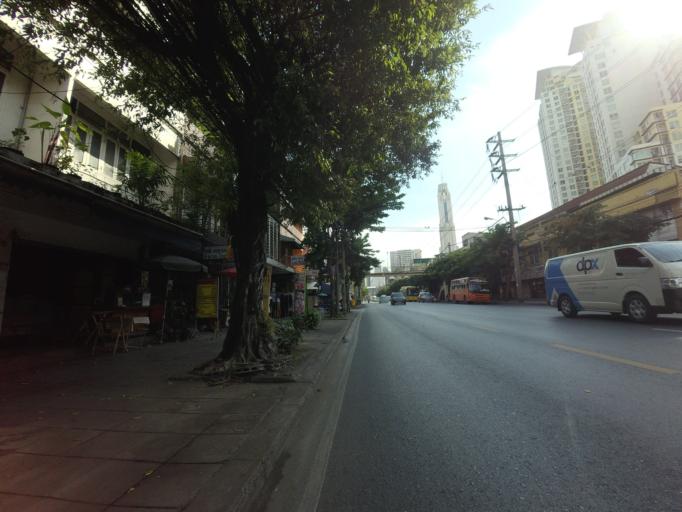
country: TH
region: Bangkok
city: Ratchathewi
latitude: 13.7616
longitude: 100.5425
